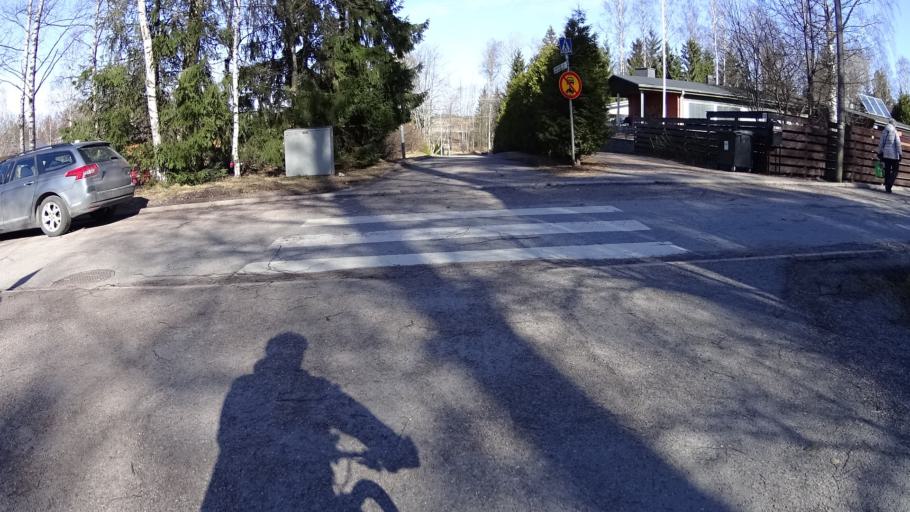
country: FI
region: Uusimaa
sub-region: Helsinki
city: Kilo
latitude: 60.1895
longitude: 24.7869
